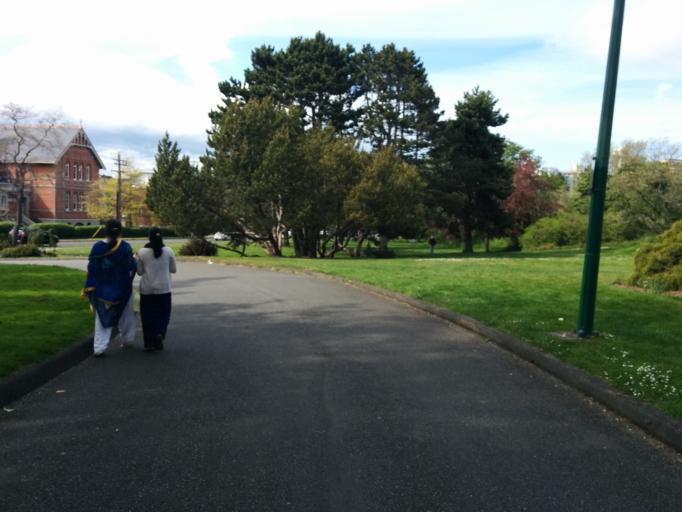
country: CA
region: British Columbia
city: Victoria
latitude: 48.4171
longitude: -123.3652
